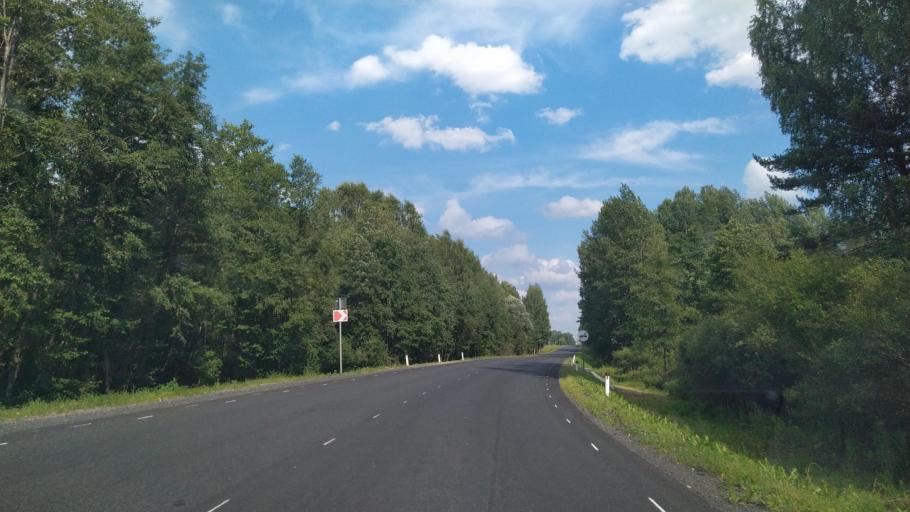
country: RU
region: Pskov
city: Porkhov
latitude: 57.7401
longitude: 29.4208
